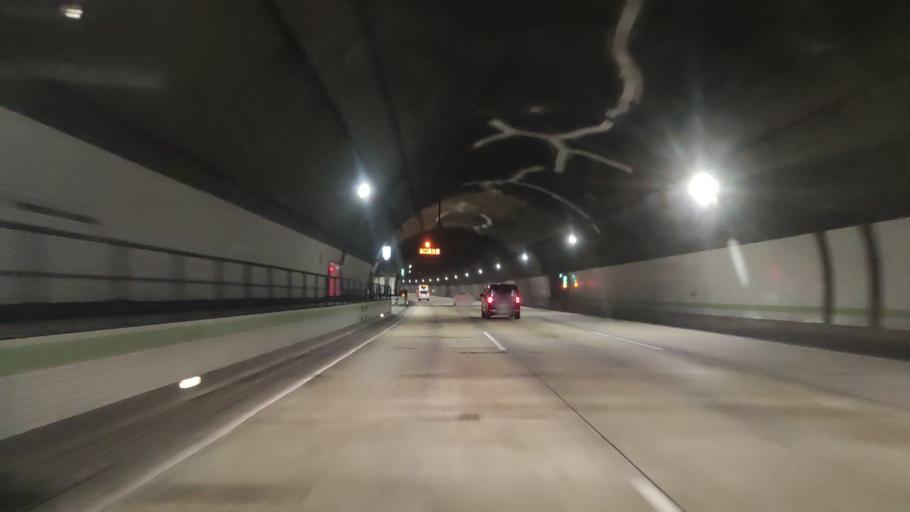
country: JP
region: Hyogo
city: Akashi
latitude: 34.6432
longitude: 135.0481
